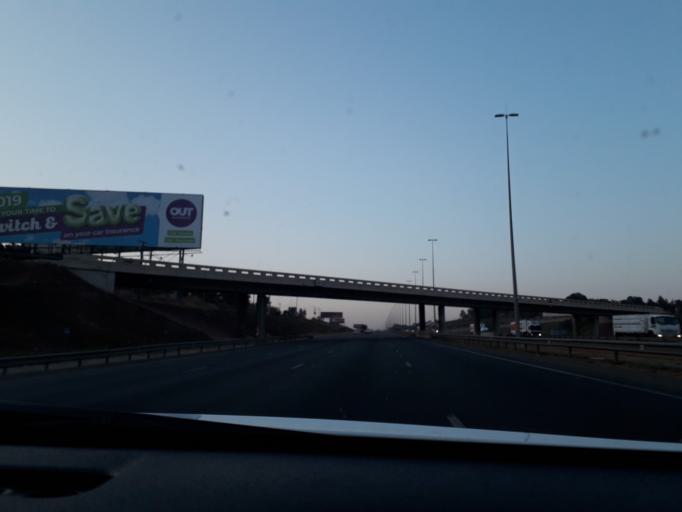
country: ZA
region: Gauteng
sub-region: City of Tshwane Metropolitan Municipality
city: Centurion
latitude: -25.8867
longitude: 28.2550
